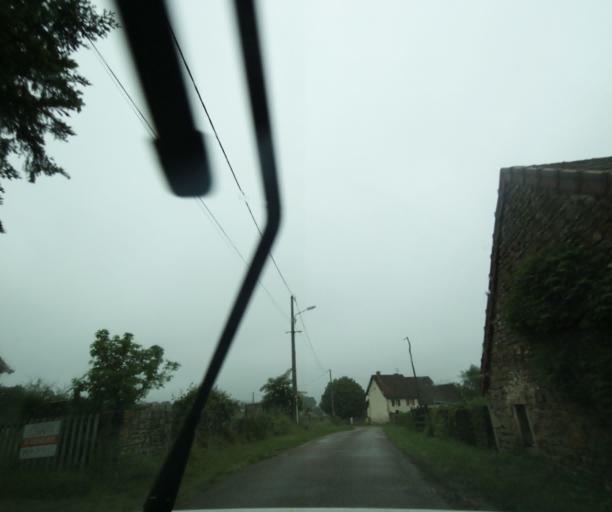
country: FR
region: Bourgogne
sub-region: Departement de Saone-et-Loire
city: Charolles
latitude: 46.3968
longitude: 4.2142
